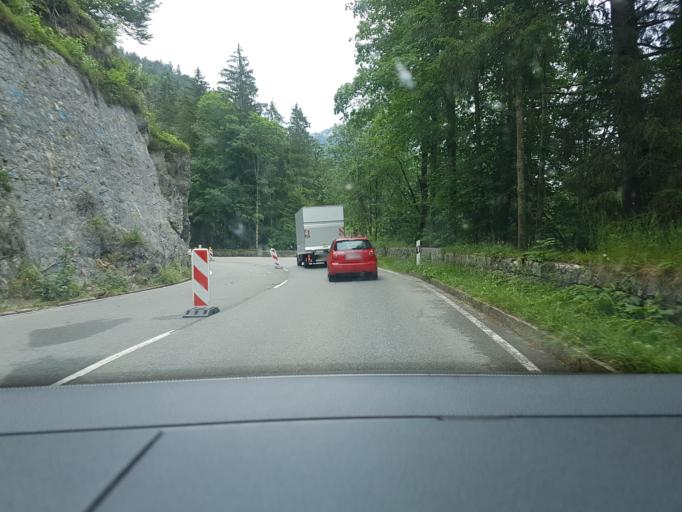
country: DE
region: Bavaria
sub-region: Upper Bavaria
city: Schneizlreuth
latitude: 47.7117
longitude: 12.7889
